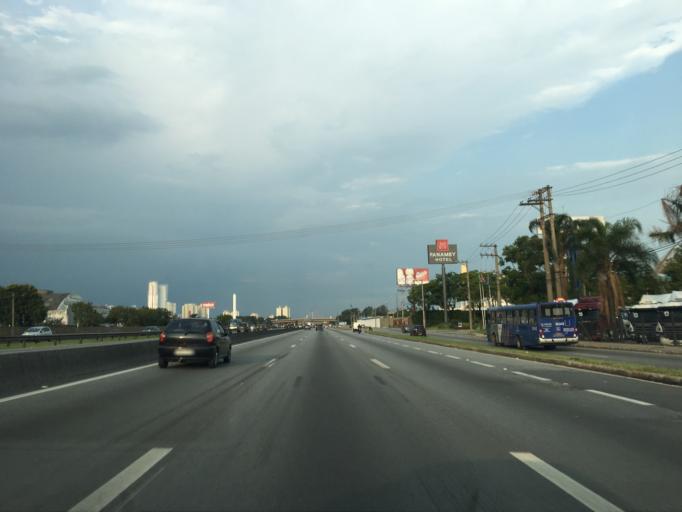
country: BR
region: Sao Paulo
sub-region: Guarulhos
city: Guarulhos
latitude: -23.4819
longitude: -46.5346
